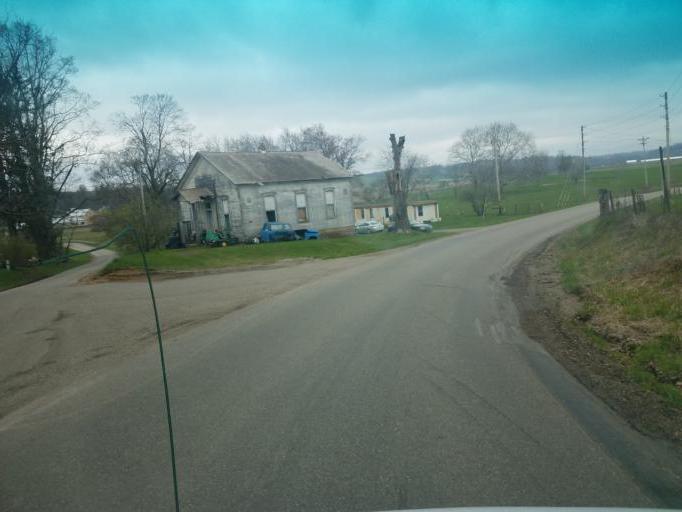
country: US
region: Ohio
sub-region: Stark County
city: Beach City
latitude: 40.5997
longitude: -81.6384
